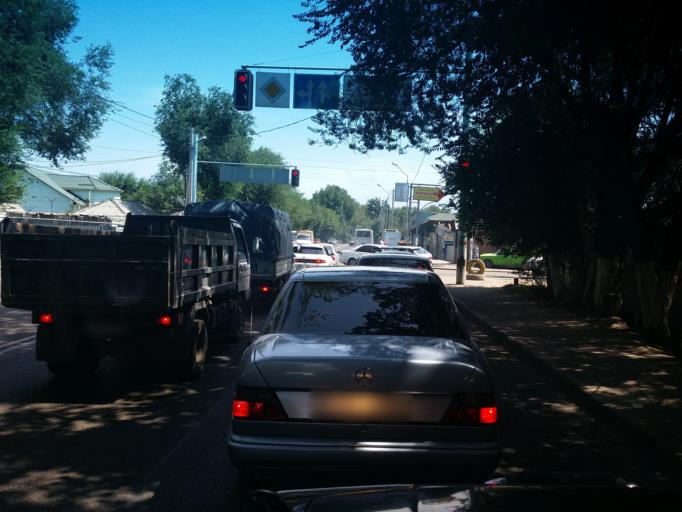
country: KZ
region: Almaty Oblysy
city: Pervomayskiy
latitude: 43.3512
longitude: 76.9596
